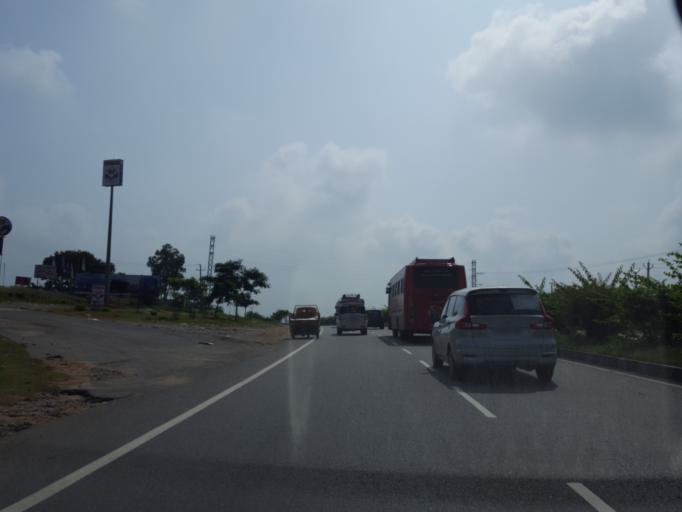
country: IN
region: Telangana
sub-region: Rangareddi
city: Ghatkesar
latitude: 17.2800
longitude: 78.7869
